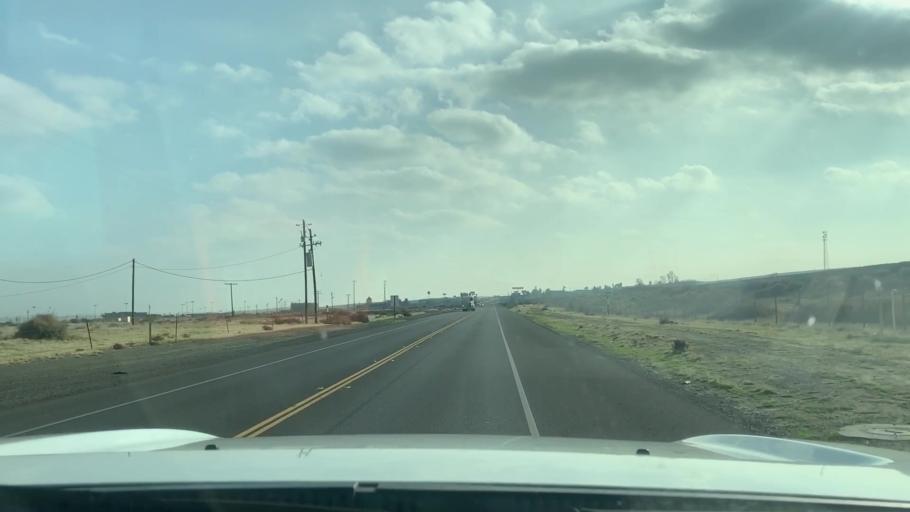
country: US
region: California
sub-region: Kings County
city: Kettleman City
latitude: 35.9972
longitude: -119.9595
